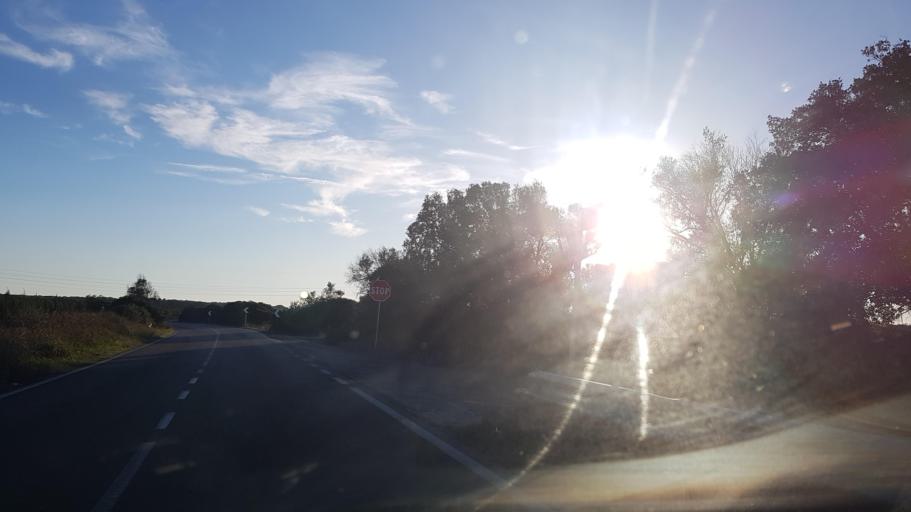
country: IT
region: Apulia
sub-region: Provincia di Lecce
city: Giorgilorio
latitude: 40.4183
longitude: 18.2073
